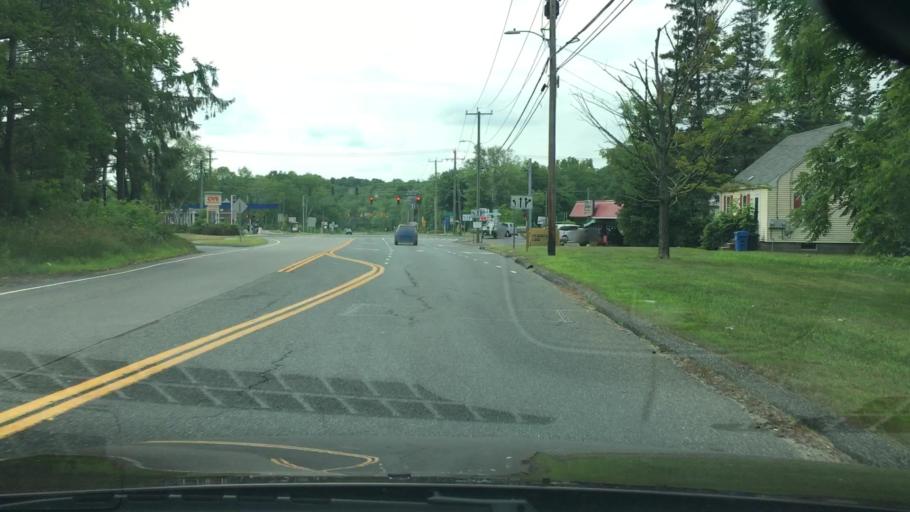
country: US
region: Connecticut
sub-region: Tolland County
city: Storrs
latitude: 41.8266
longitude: -72.2655
